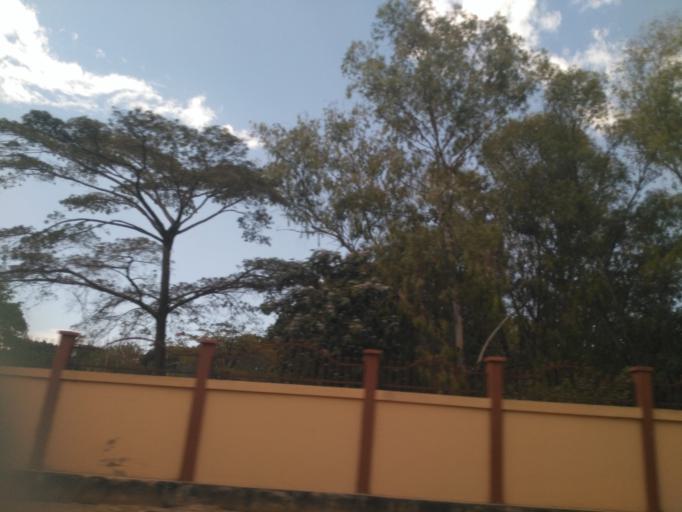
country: TZ
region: Mwanza
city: Mwanza
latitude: -2.5143
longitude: 32.9063
